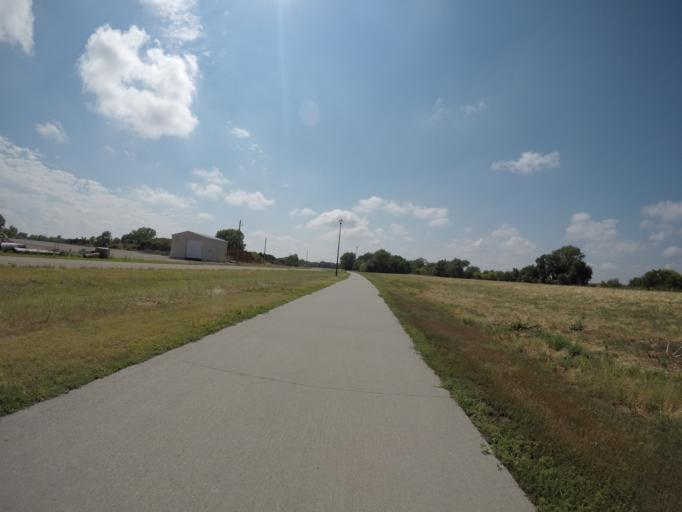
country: US
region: Nebraska
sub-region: Buffalo County
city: Kearney
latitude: 40.6745
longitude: -99.0566
